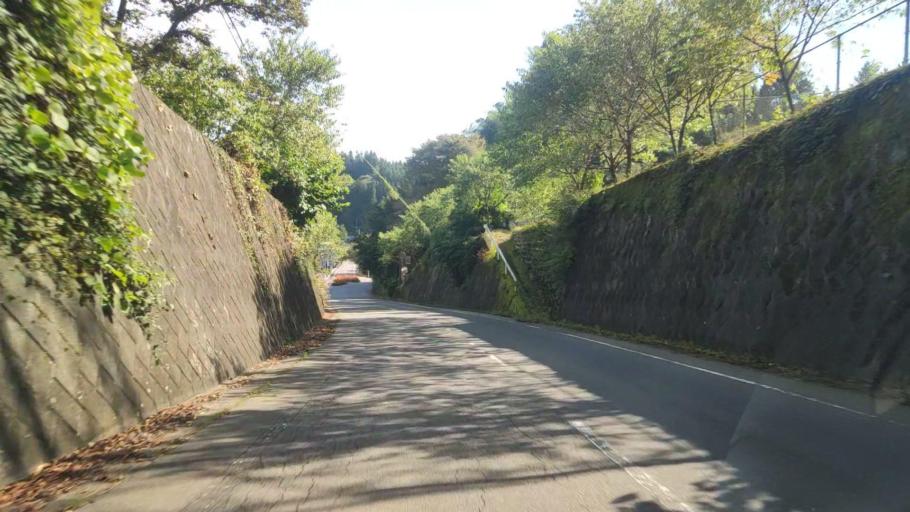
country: JP
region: Gunma
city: Nakanojomachi
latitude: 36.6201
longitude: 138.7605
